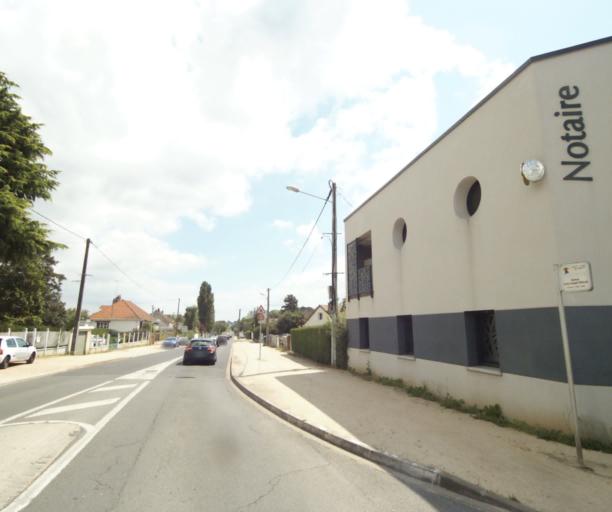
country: FR
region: Centre
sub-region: Departement du Loiret
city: Saint-Jean-de-Braye
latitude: 47.9076
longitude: 1.9627
